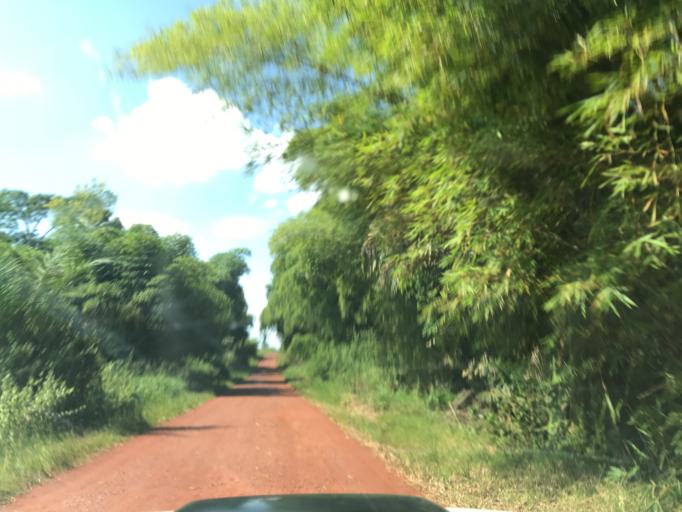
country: CD
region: Eastern Province
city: Kisangani
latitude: 1.2112
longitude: 25.2652
